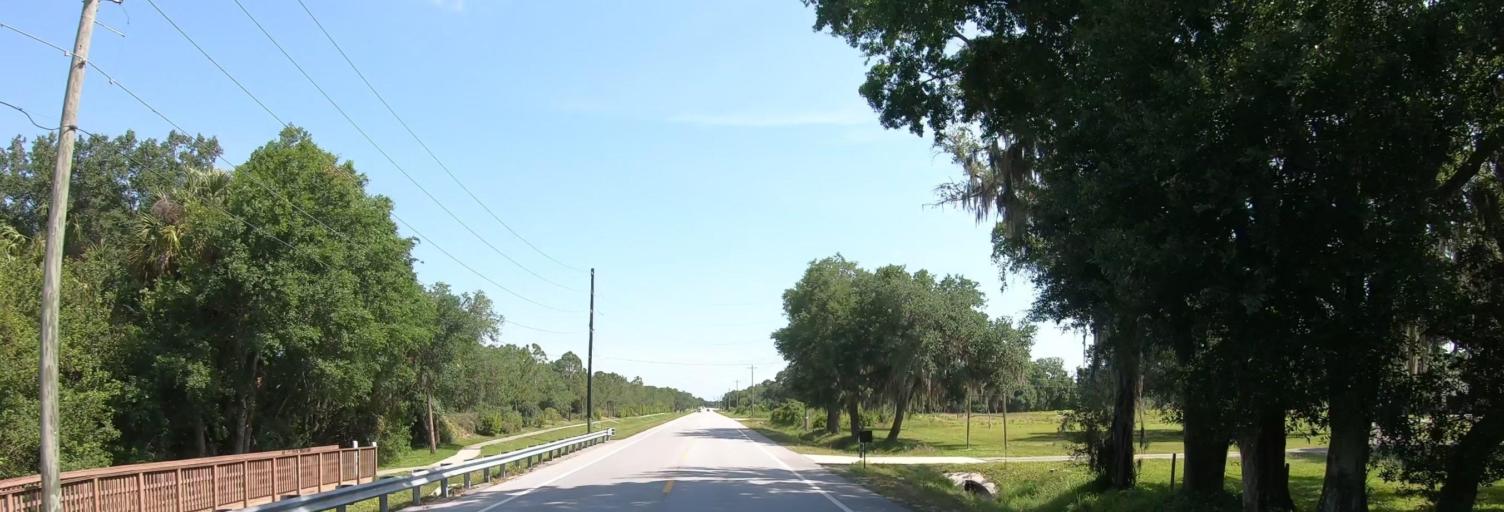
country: US
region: Florida
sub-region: Manatee County
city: Ellenton
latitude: 27.5291
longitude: -82.4284
